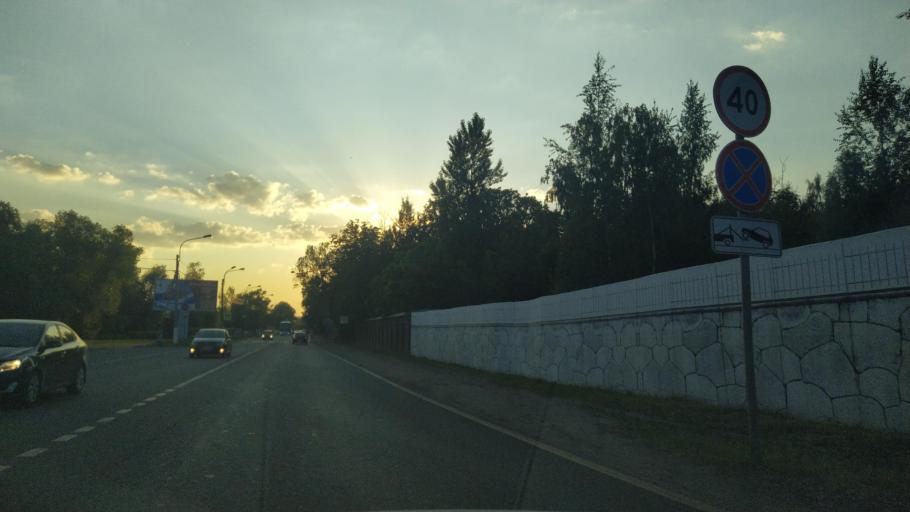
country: RU
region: St.-Petersburg
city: Kronshtadt
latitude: 60.0027
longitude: 29.7576
